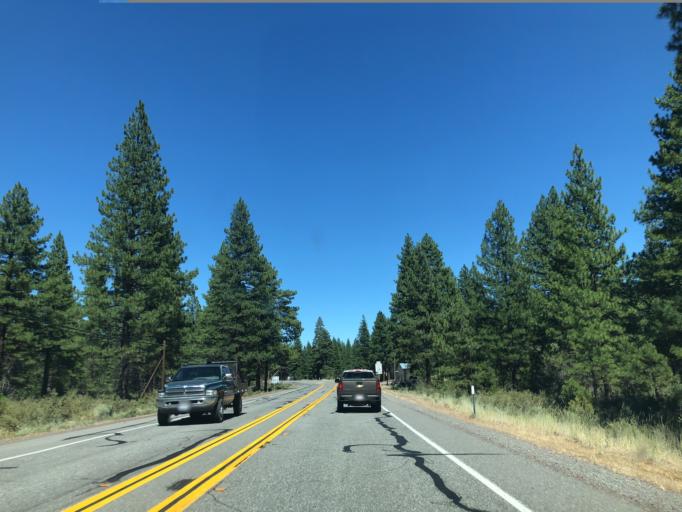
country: US
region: California
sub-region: Lassen County
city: Susanville
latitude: 40.4191
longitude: -120.7067
